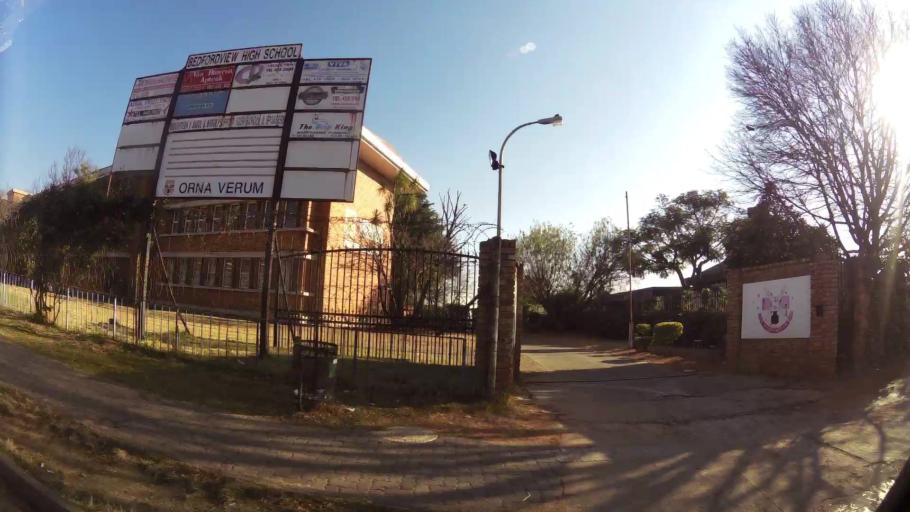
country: ZA
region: Gauteng
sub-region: Ekurhuleni Metropolitan Municipality
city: Germiston
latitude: -26.1959
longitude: 28.1287
